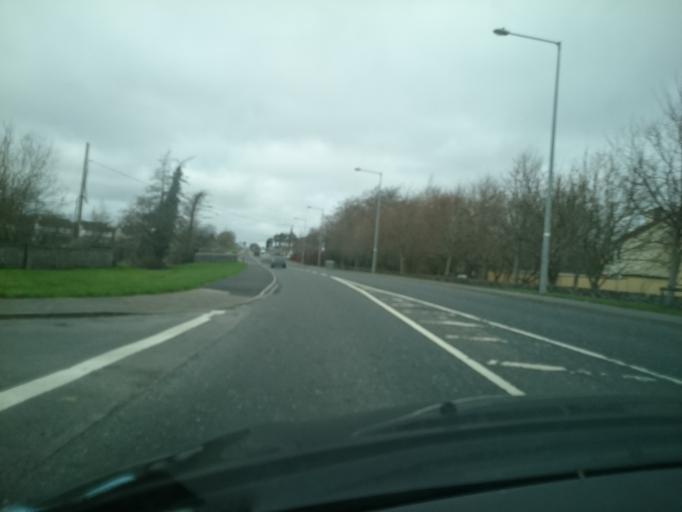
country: IE
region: Connaught
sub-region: Maigh Eo
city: Kiltamagh
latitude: 53.8076
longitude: -9.1327
